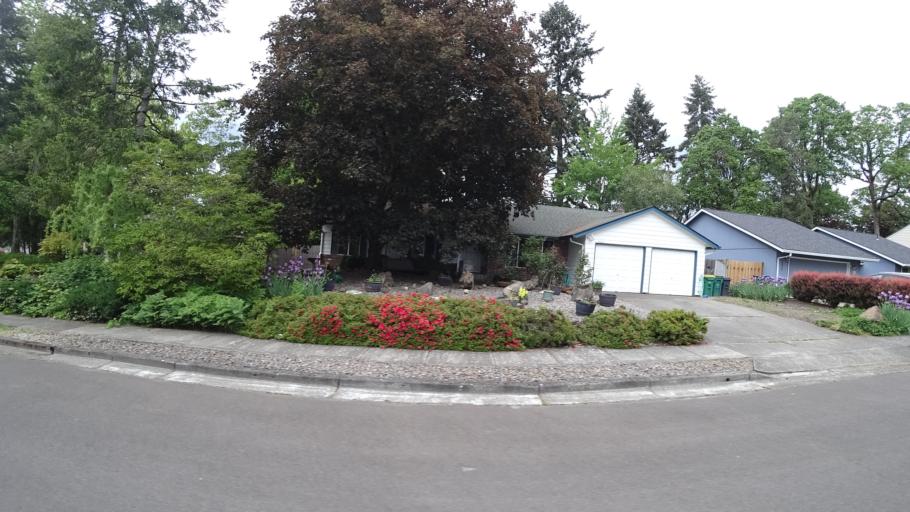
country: US
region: Oregon
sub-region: Washington County
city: Beaverton
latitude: 45.4783
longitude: -122.8291
